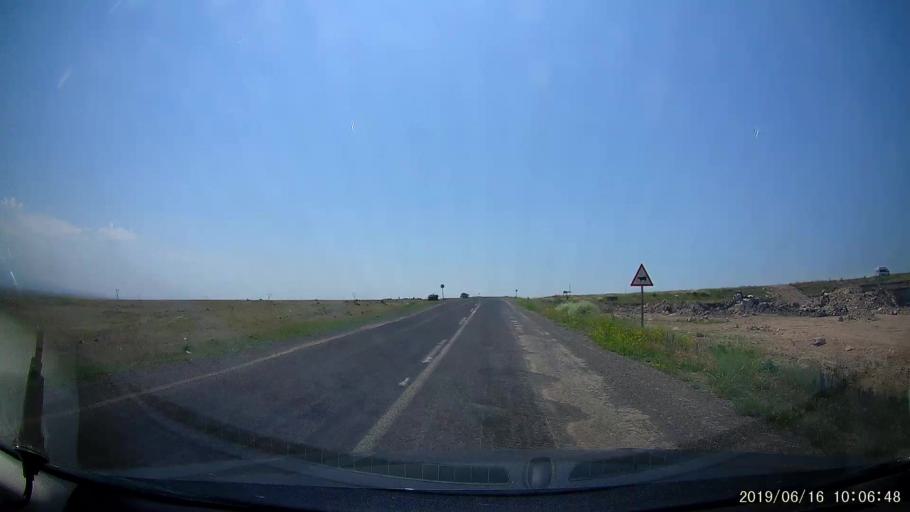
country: TR
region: Kars
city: Digor
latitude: 40.2511
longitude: 43.5468
